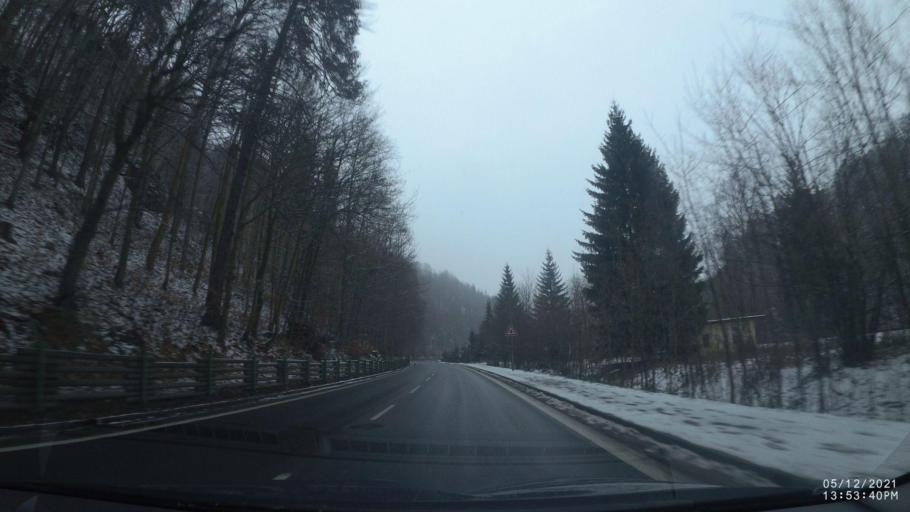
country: CZ
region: Kralovehradecky
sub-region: Okres Nachod
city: Police nad Metuji
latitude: 50.5154
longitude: 16.2120
